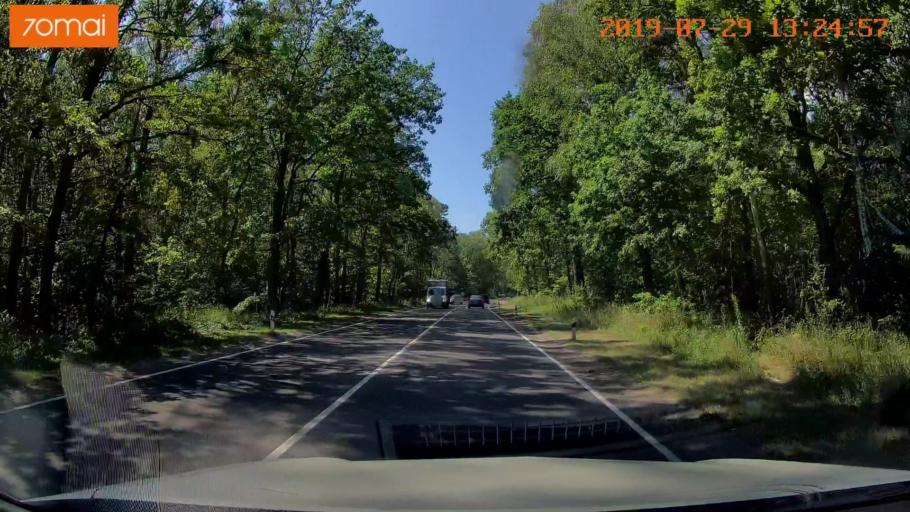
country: RU
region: Kaliningrad
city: Vzmorye
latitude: 54.7119
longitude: 20.3392
